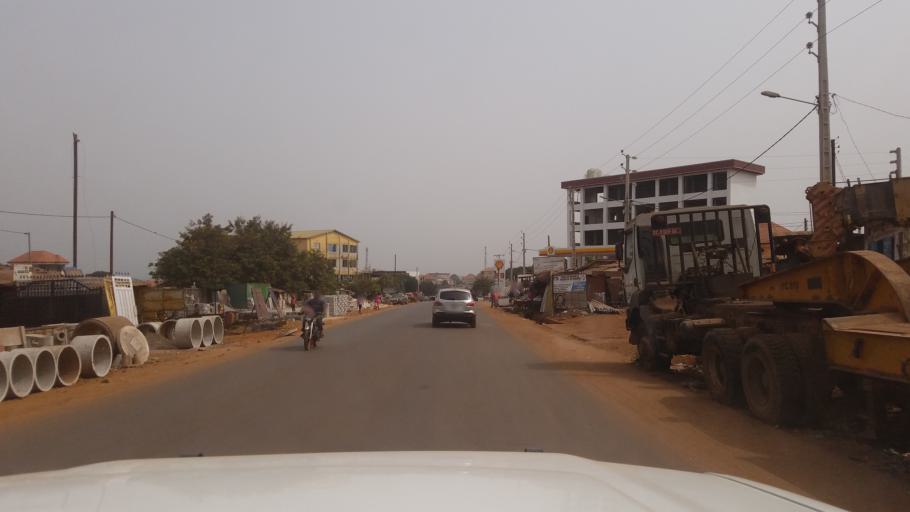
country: GN
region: Conakry
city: Conakry
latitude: 9.6598
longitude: -13.5976
